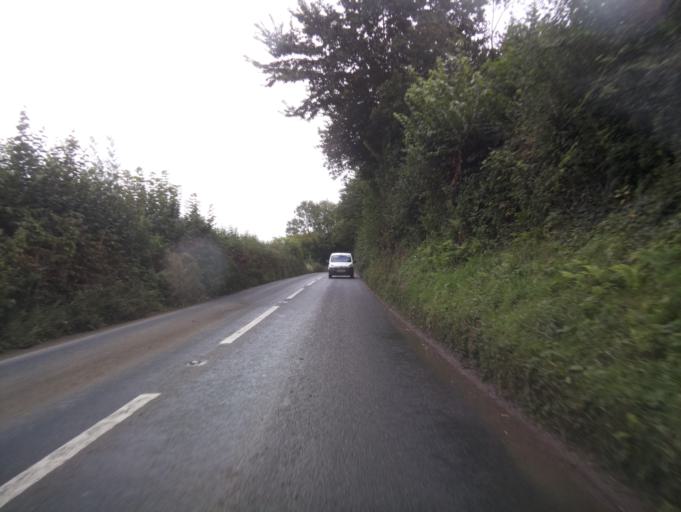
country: GB
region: England
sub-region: Devon
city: Modbury
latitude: 50.3335
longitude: -3.8496
